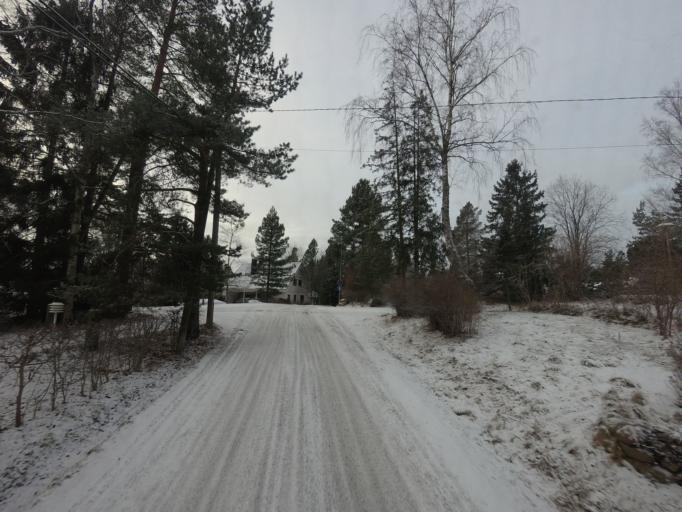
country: FI
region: Uusimaa
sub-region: Helsinki
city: Espoo
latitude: 60.2051
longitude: 24.6902
